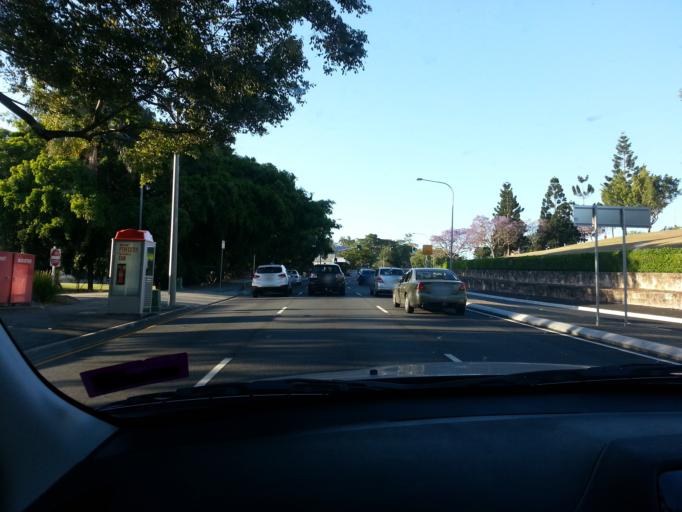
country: AU
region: Queensland
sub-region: Brisbane
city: Windsor
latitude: -27.4319
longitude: 153.0319
